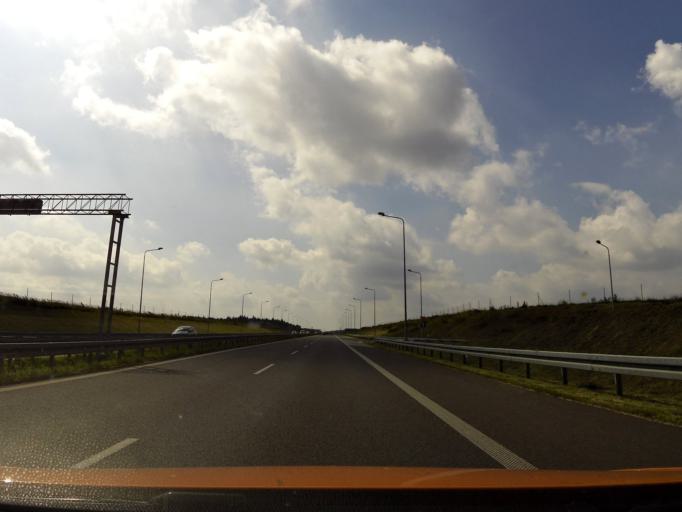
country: PL
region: West Pomeranian Voivodeship
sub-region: Powiat goleniowski
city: Nowogard
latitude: 53.6841
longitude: 15.0878
